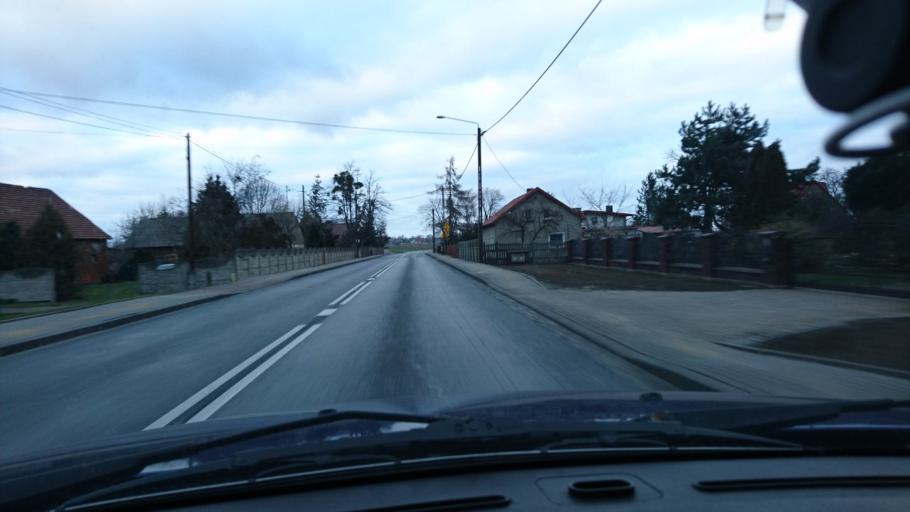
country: PL
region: Greater Poland Voivodeship
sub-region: Powiat kepinski
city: Opatow
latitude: 51.1686
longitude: 18.1467
